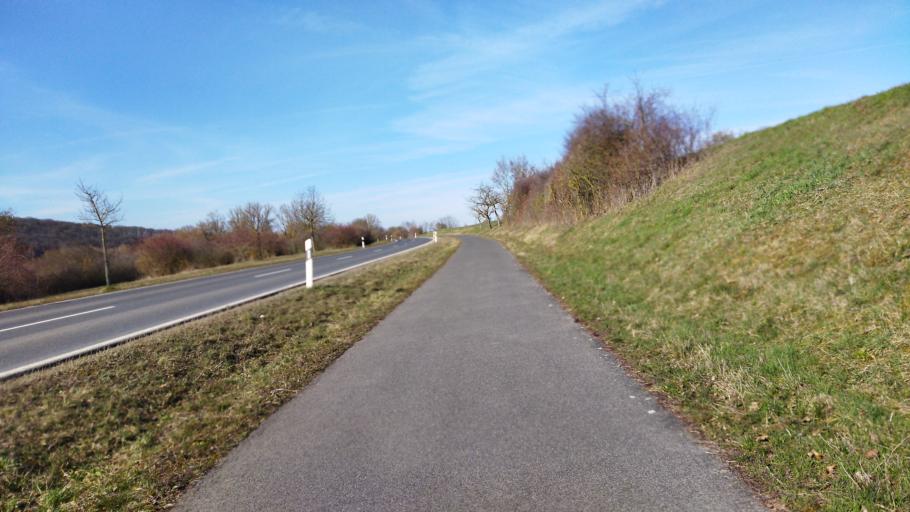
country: DE
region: Bavaria
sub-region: Regierungsbezirk Unterfranken
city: Wipfeld
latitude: 49.9299
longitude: 10.1838
